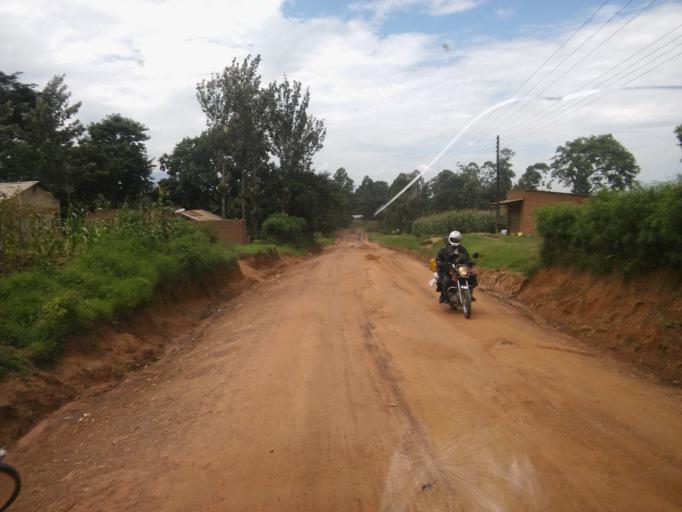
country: KE
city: Malikisi
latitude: 0.8143
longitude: 34.3267
